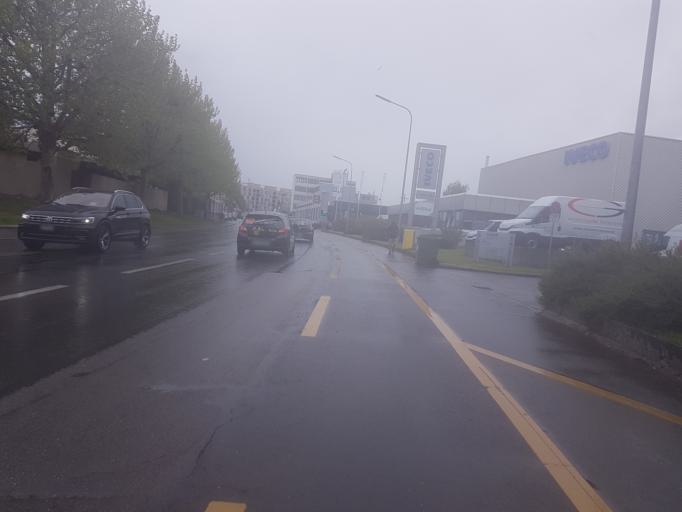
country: CH
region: Vaud
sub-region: Morges District
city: Morges
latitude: 46.5166
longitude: 6.5074
